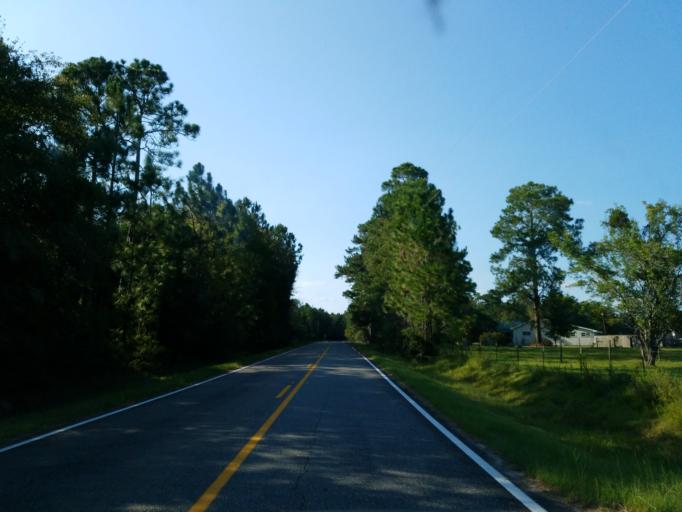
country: US
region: Georgia
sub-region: Lowndes County
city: Hahira
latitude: 31.0260
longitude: -83.3908
